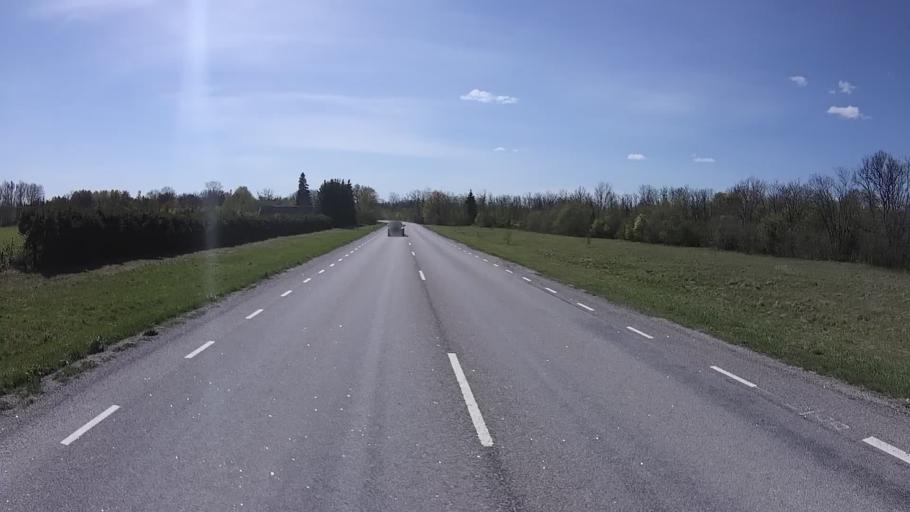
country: EE
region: Laeaene
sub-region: Ridala Parish
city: Uuemoisa
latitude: 58.9762
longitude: 23.6794
